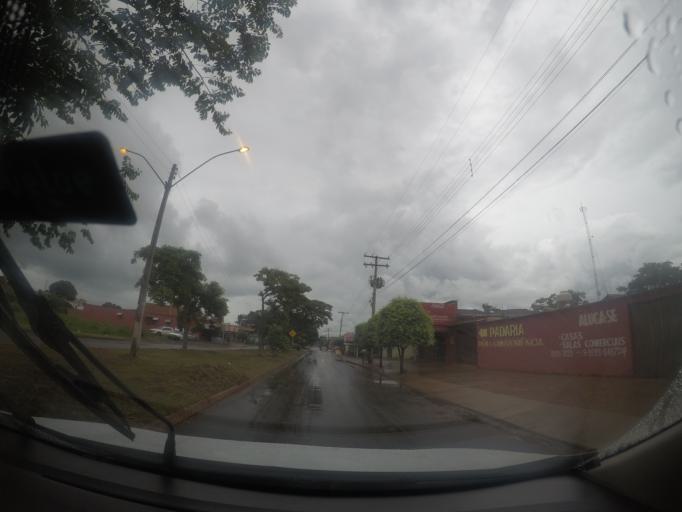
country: BR
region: Goias
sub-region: Trindade
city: Trindade
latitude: -16.6422
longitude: -49.4350
